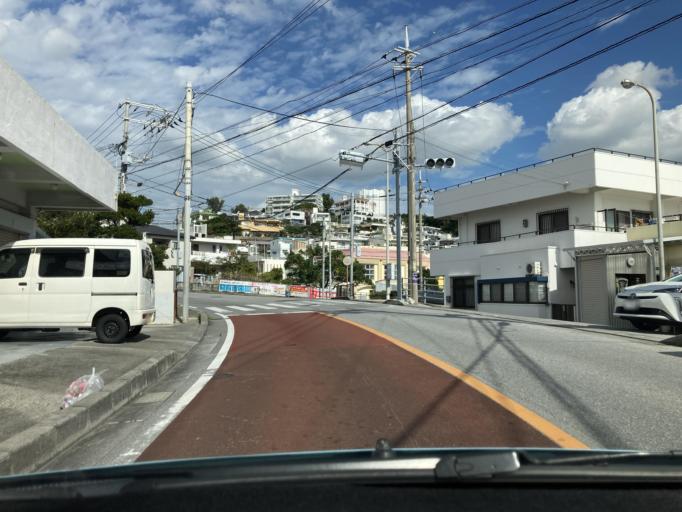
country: JP
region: Okinawa
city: Chatan
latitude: 26.3146
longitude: 127.7720
